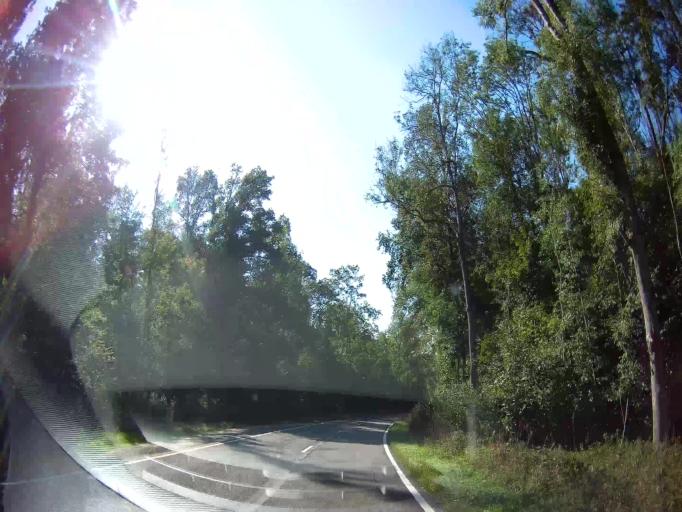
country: BE
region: Wallonia
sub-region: Province de Namur
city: Dinant
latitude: 50.2446
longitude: 4.9586
